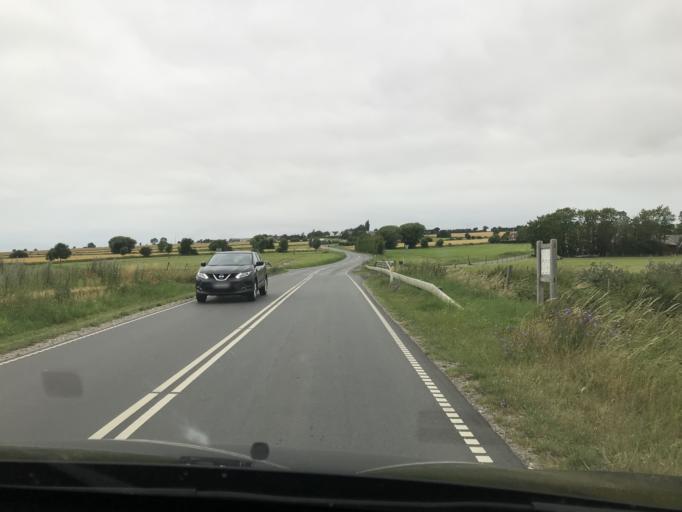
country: DK
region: South Denmark
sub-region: AEro Kommune
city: AEroskobing
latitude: 54.8406
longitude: 10.4394
